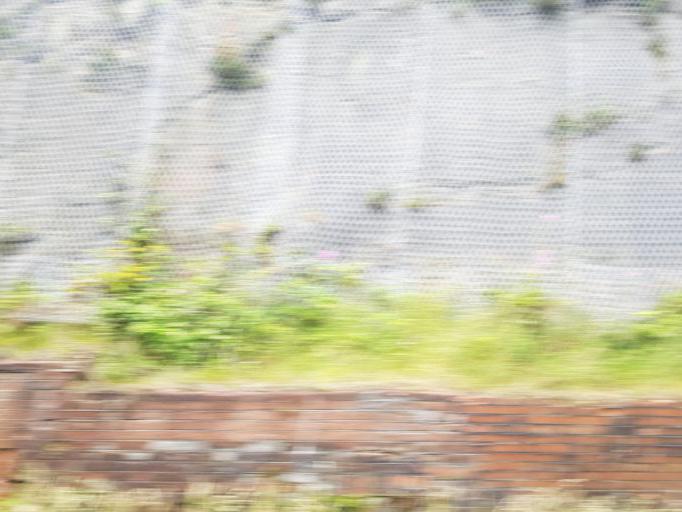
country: GB
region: Scotland
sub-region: East Dunbartonshire
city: Bishopbriggs
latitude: 55.8958
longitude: -4.2378
